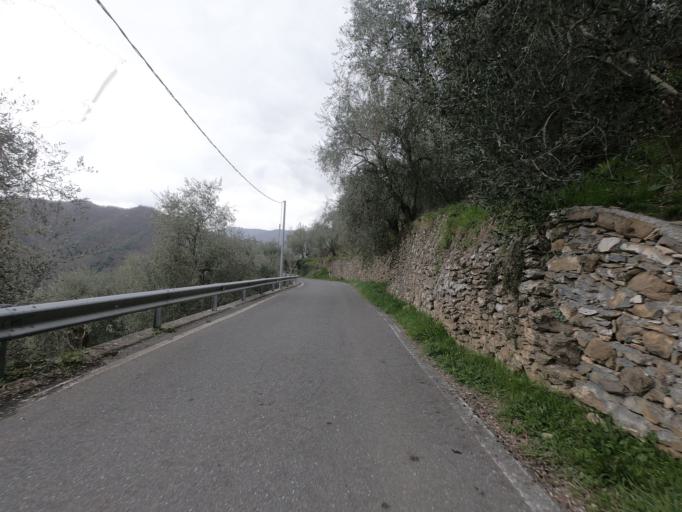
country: IT
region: Liguria
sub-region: Provincia di Savona
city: Testico
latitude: 44.0306
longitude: 8.0217
